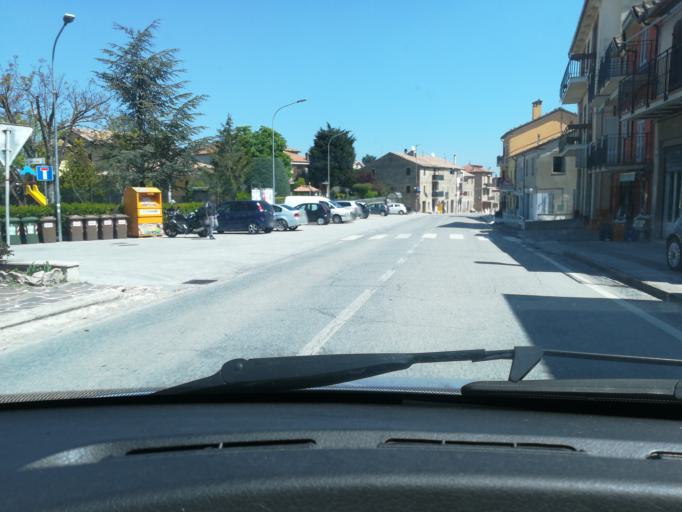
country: IT
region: The Marches
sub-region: Provincia di Macerata
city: Strada
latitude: 43.3976
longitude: 13.2086
